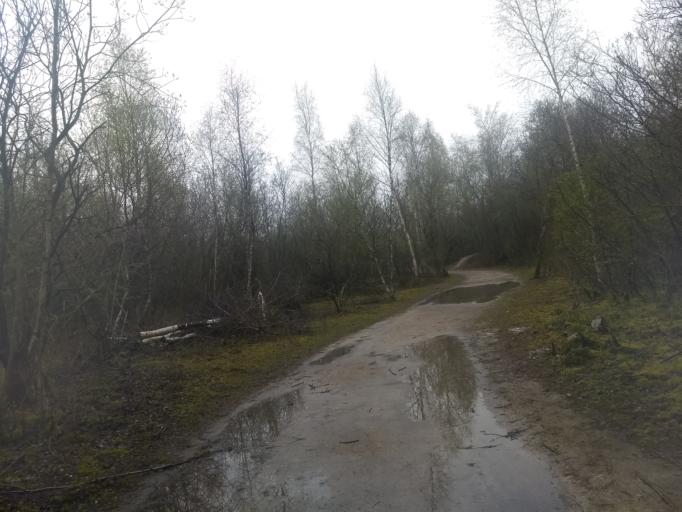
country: FR
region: Nord-Pas-de-Calais
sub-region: Departement du Pas-de-Calais
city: Roeux
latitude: 50.2975
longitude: 2.9207
